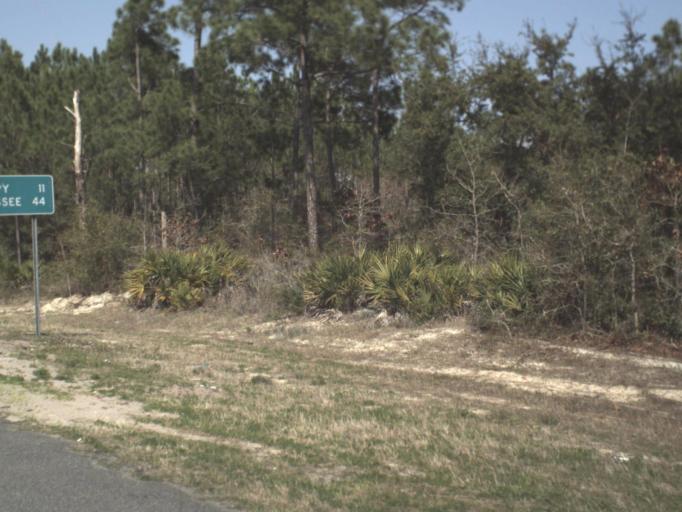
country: US
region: Florida
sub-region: Franklin County
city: Carrabelle
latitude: 29.9204
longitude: -84.5203
